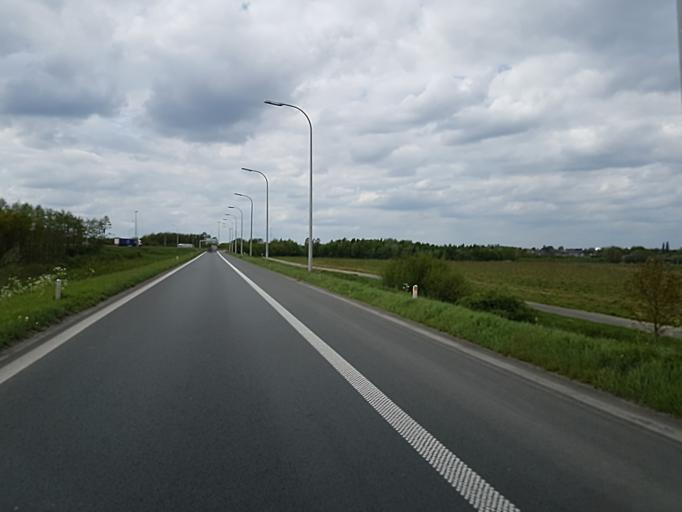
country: BE
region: Flanders
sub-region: Provincie West-Vlaanderen
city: Kortrijk
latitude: 50.7915
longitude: 3.2297
